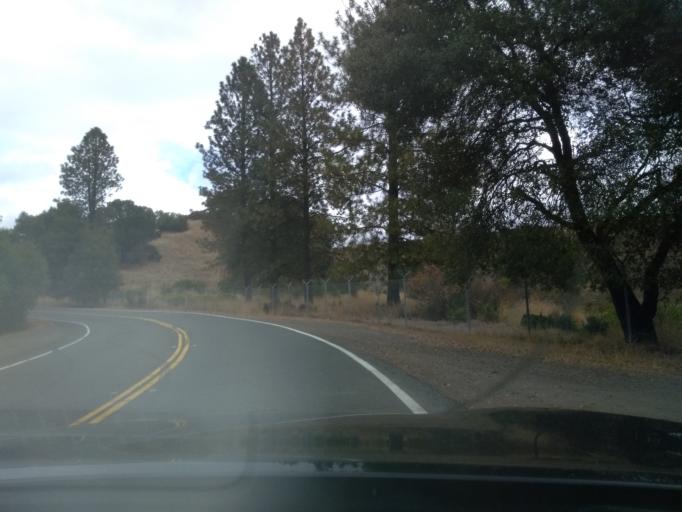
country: US
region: California
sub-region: Mendocino County
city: Ukiah
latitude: 39.1994
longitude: -123.1859
